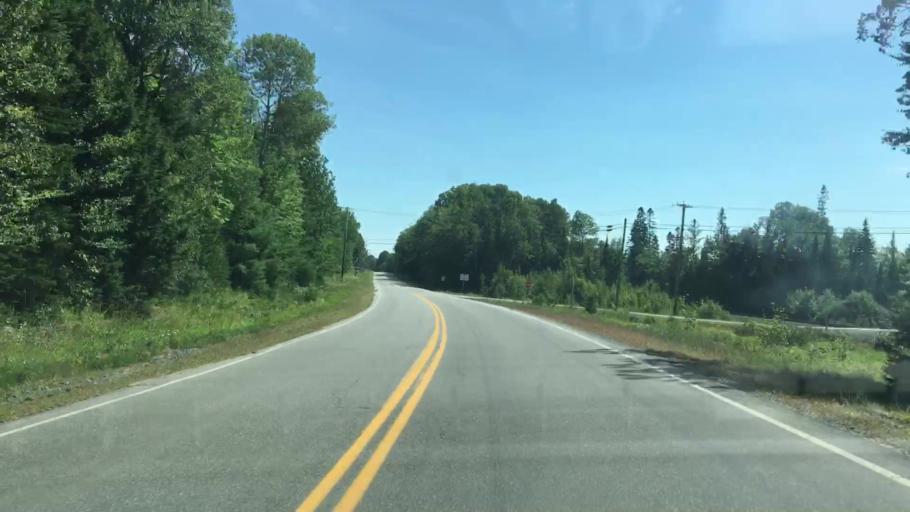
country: US
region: Maine
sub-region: Piscataquis County
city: Milo
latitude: 45.1999
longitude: -68.9063
